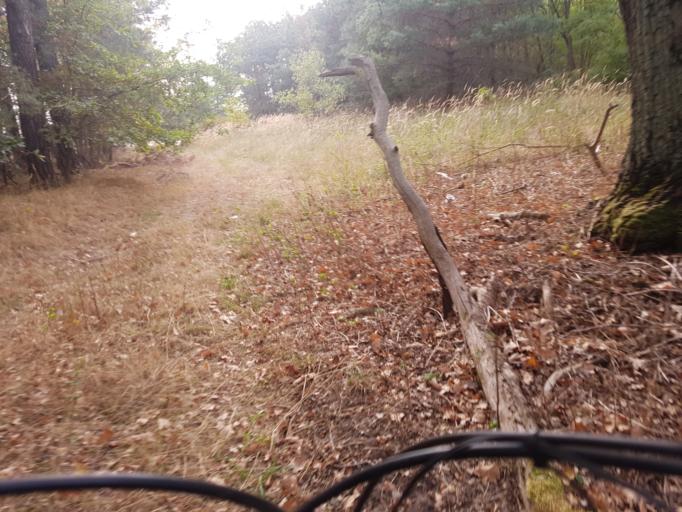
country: DE
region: Brandenburg
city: Schilda
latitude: 51.5868
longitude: 13.3726
